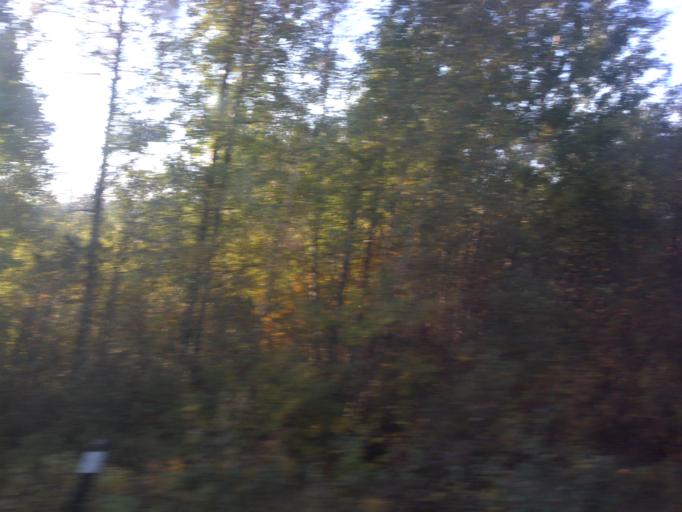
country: RU
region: St.-Petersburg
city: Krasnogvargeisky
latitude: 59.9777
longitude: 30.5389
